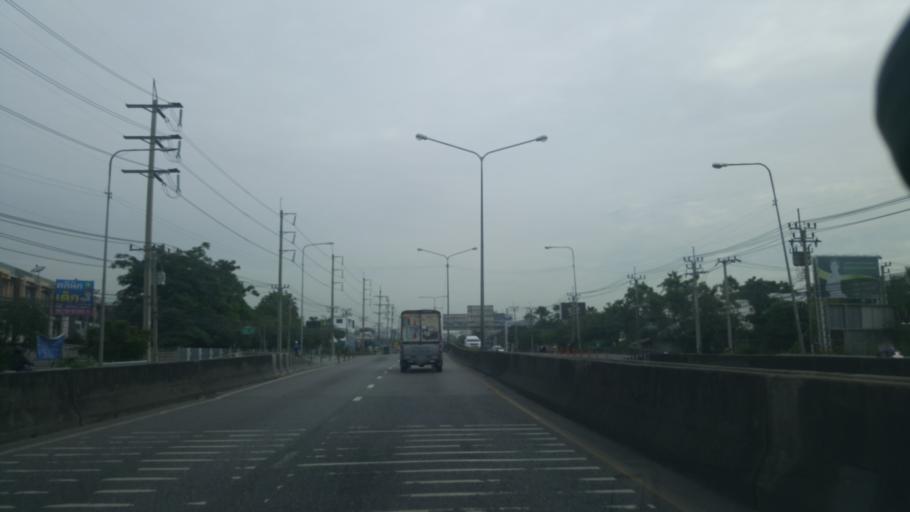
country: TH
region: Bangkok
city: Phasi Charoen
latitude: 13.6961
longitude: 100.4389
